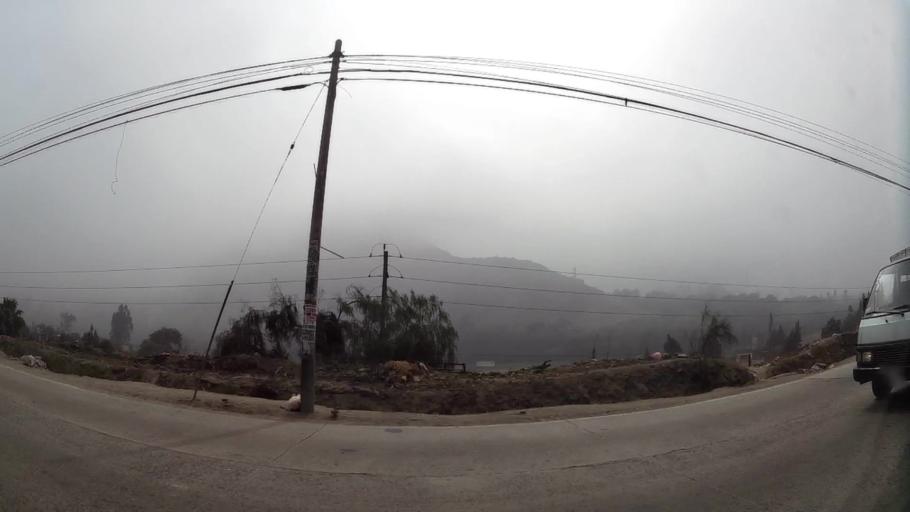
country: PE
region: Lima
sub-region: Lima
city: Chaclacayo
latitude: -11.9724
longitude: -76.7572
